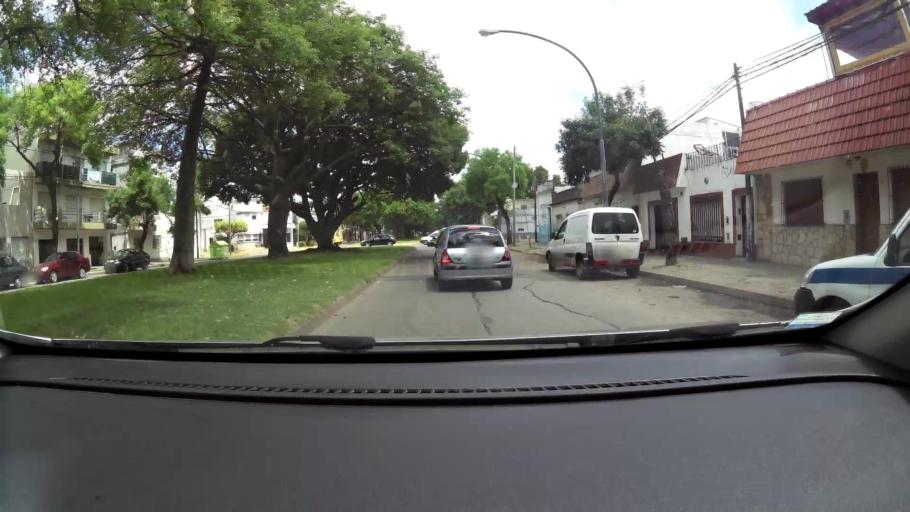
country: AR
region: Santa Fe
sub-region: Departamento de Rosario
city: Rosario
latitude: -32.9803
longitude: -60.6389
